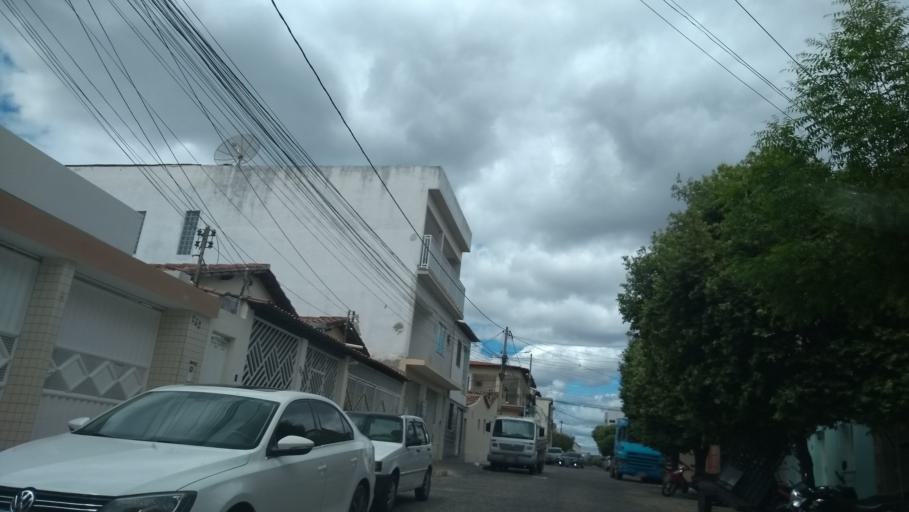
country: BR
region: Bahia
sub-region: Brumado
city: Brumado
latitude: -14.2095
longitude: -41.6749
